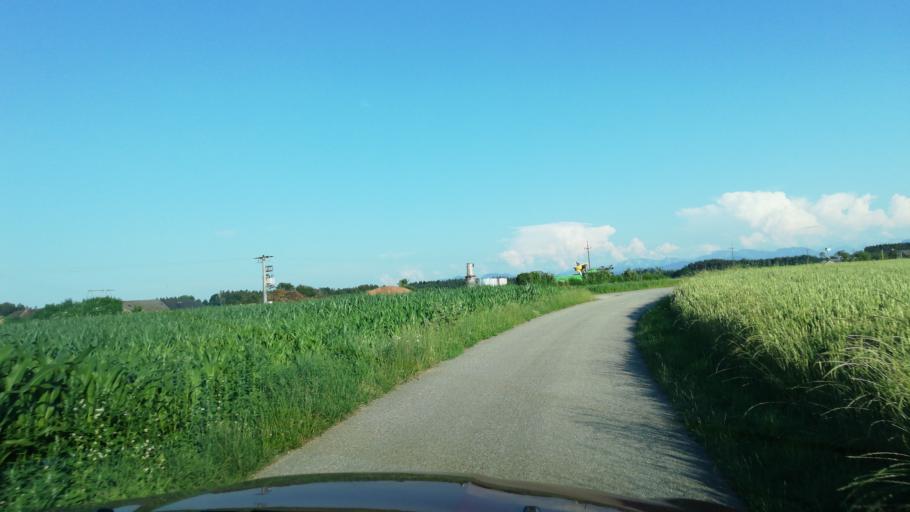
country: AT
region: Upper Austria
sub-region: Wels-Land
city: Sattledt
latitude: 48.0793
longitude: 14.0324
